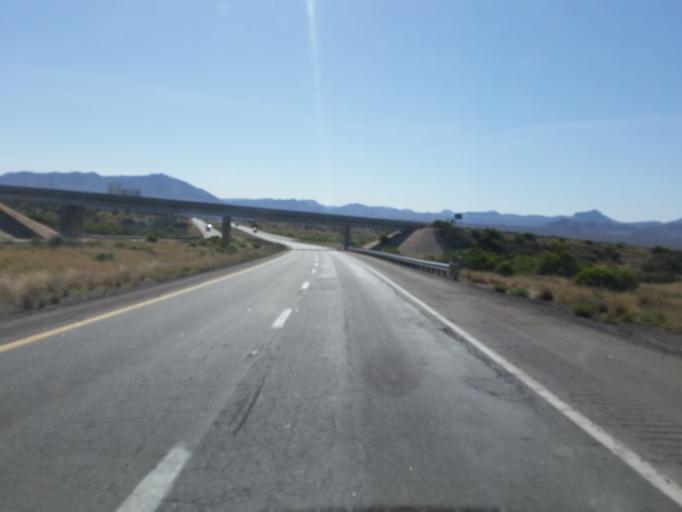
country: US
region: Arizona
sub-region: Mohave County
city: New Kingman-Butler
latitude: 35.1592
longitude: -113.6980
